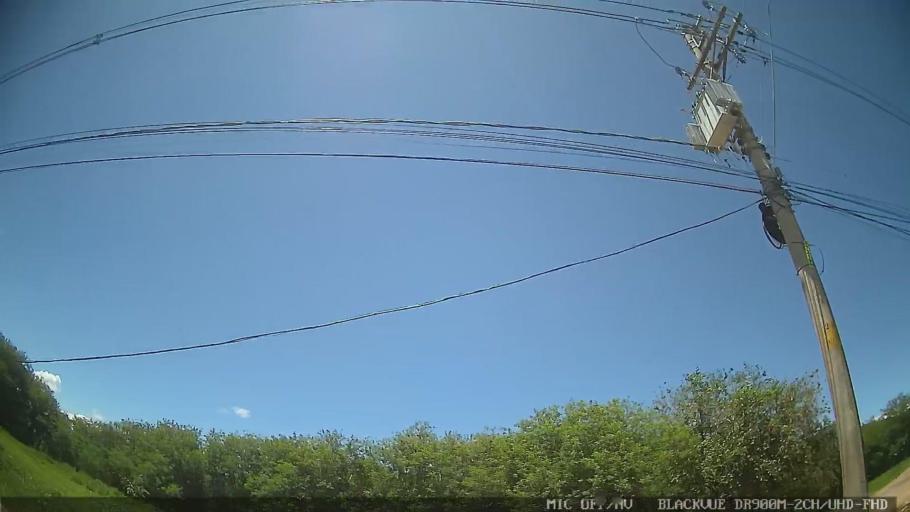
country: BR
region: Sao Paulo
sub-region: Pedreira
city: Pedreira
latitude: -22.7415
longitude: -46.9224
